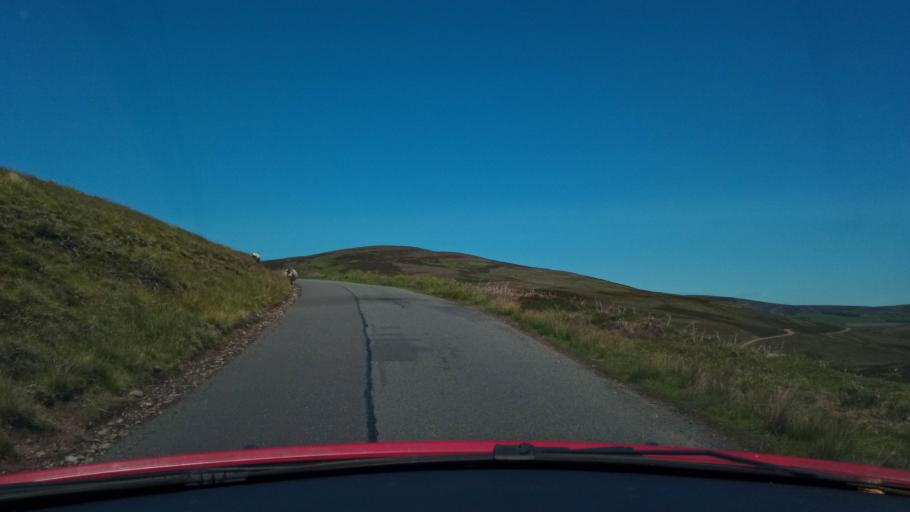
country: GB
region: Scotland
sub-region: East Lothian
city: East Linton
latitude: 55.8433
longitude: -2.5835
